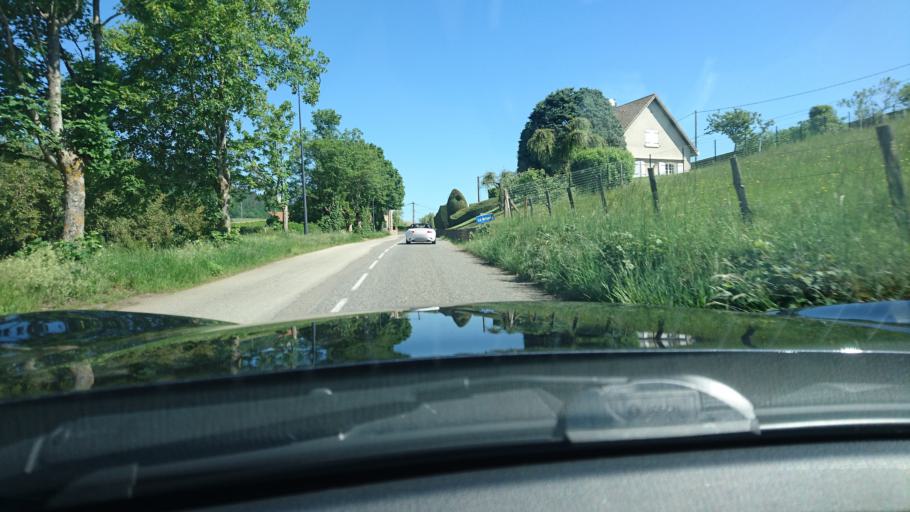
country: FR
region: Rhone-Alpes
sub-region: Departement de la Loire
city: Violay
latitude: 45.8157
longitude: 4.4048
